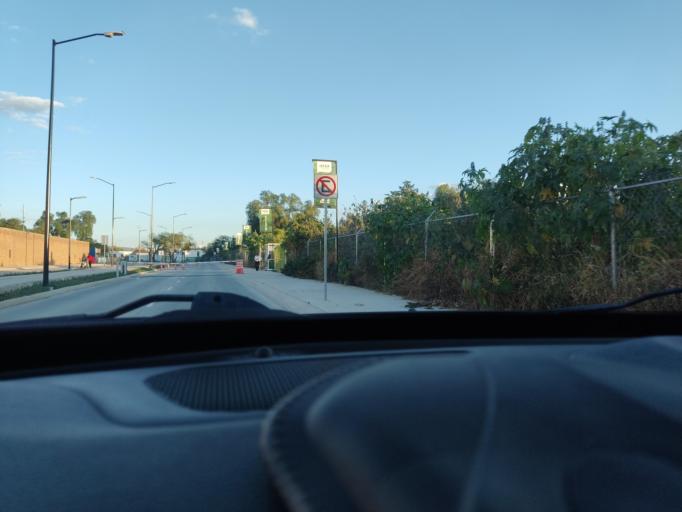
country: MX
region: Guanajuato
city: Leon
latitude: 21.1569
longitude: -101.6655
